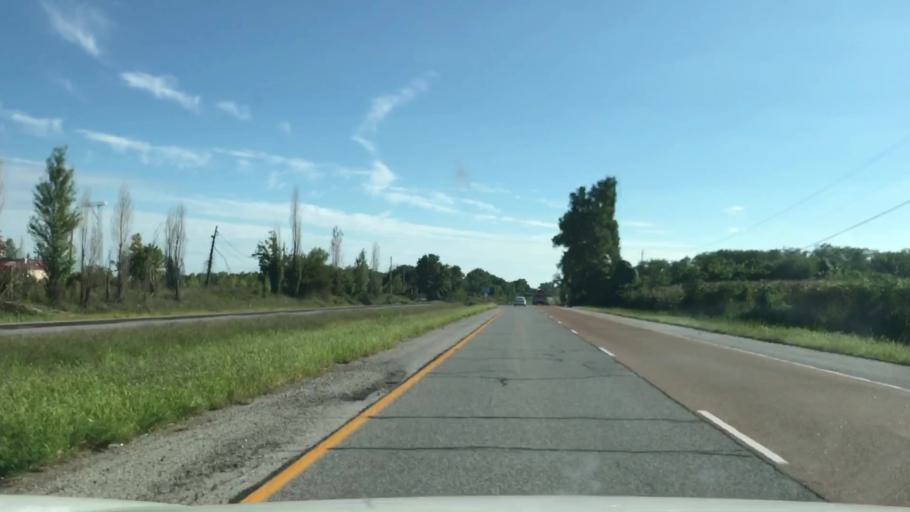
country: US
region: Illinois
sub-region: Madison County
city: Hartford
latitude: 38.7987
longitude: -90.1013
